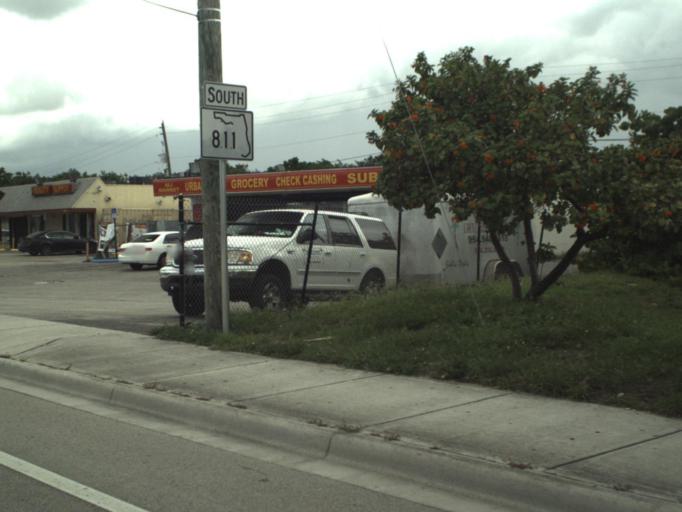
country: US
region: Florida
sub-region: Broward County
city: Pompano Beach Highlands
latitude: 26.2970
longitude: -80.1076
